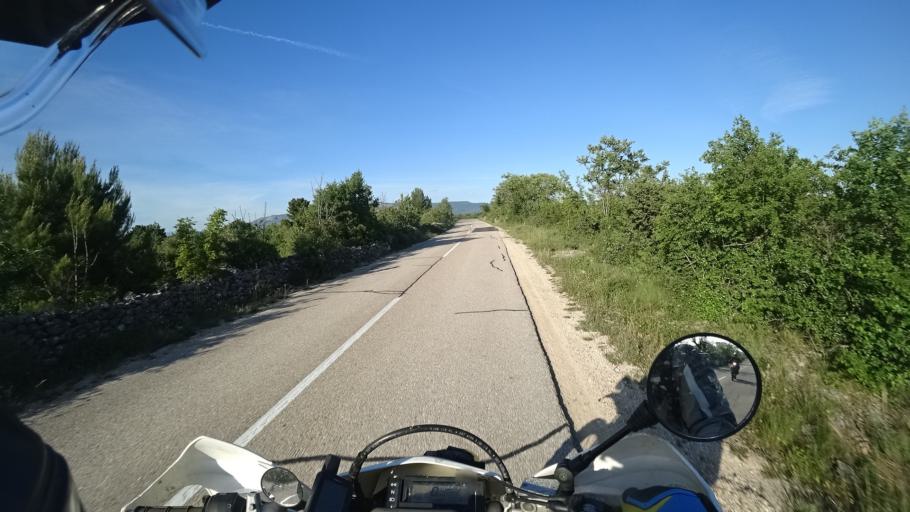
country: HR
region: Sibensko-Kniniska
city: Drnis
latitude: 43.8515
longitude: 16.0620
